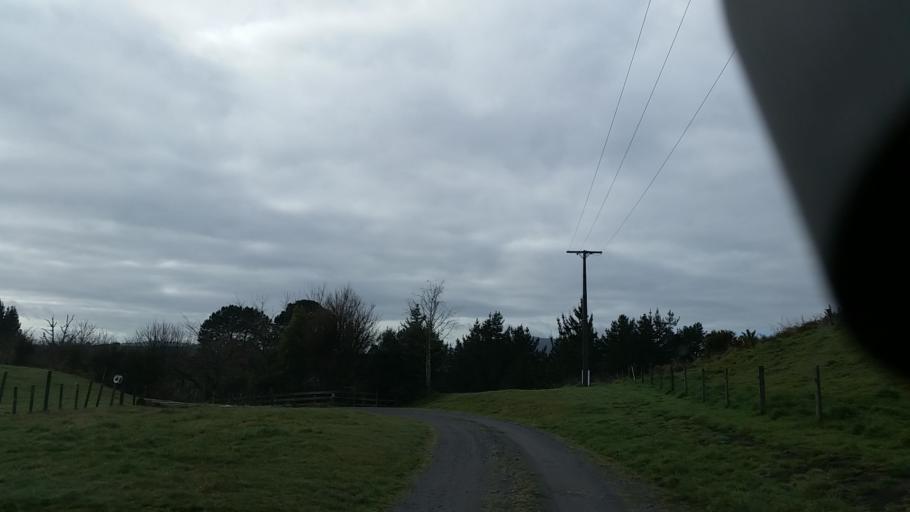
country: NZ
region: Bay of Plenty
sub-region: Rotorua District
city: Rotorua
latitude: -38.2389
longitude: 176.2315
